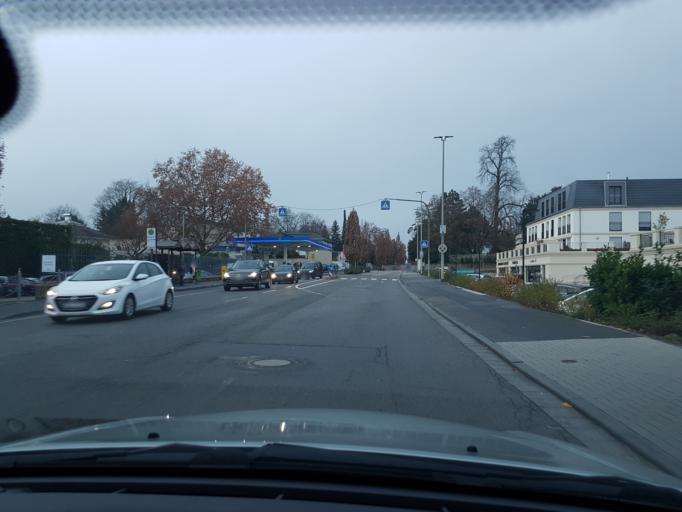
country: DE
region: Hesse
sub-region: Regierungsbezirk Darmstadt
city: Eltville
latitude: 50.0247
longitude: 8.1171
